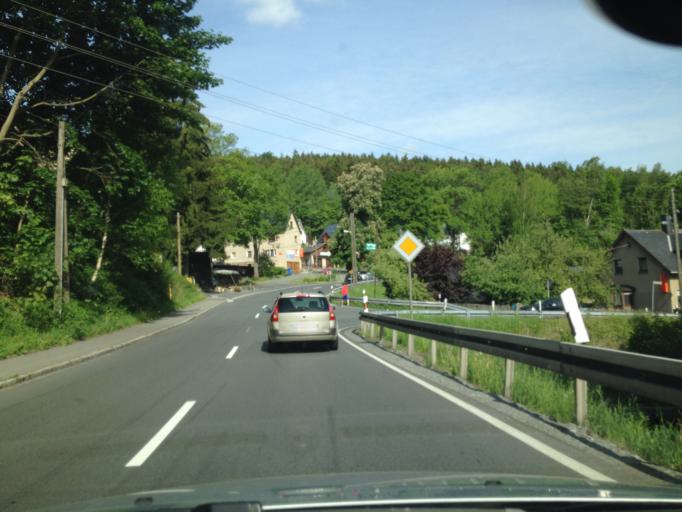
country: DE
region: Saxony
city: Ehrenfriedersdorf
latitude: 50.6620
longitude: 12.9660
